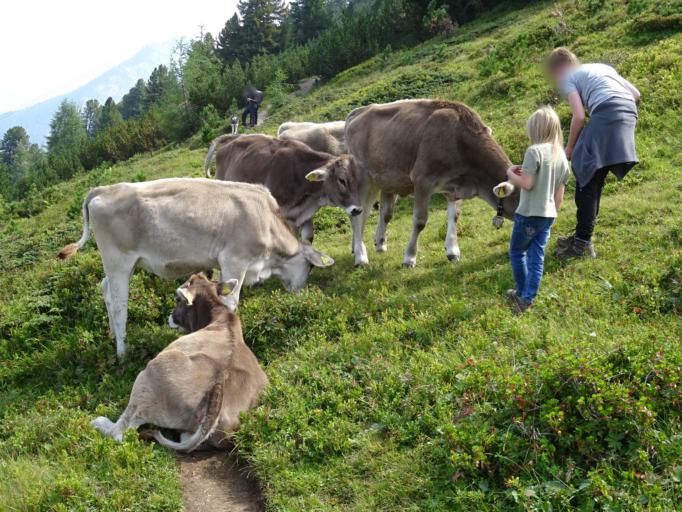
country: AT
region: Styria
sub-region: Politischer Bezirk Liezen
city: Aich
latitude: 47.4602
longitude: 13.8221
